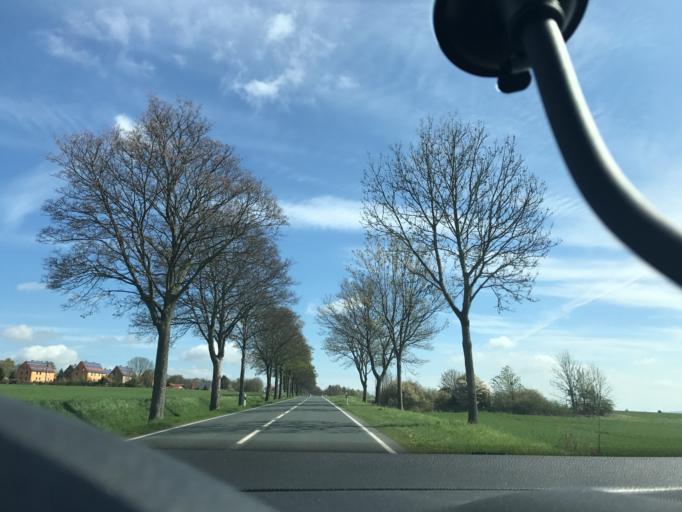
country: DE
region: Lower Saxony
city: Twieflingen
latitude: 52.1331
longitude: 10.9354
